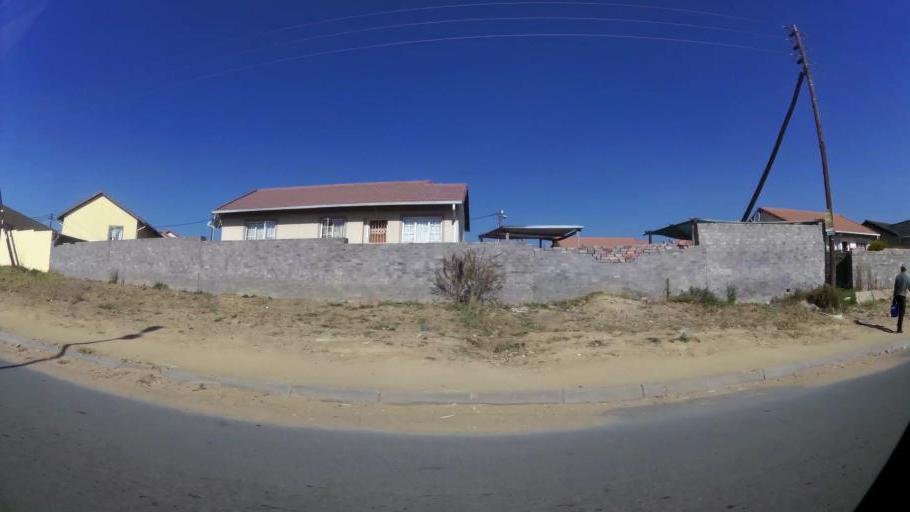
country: ZA
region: Gauteng
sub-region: West Rand District Municipality
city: Muldersdriseloop
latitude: -26.0363
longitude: 27.9236
